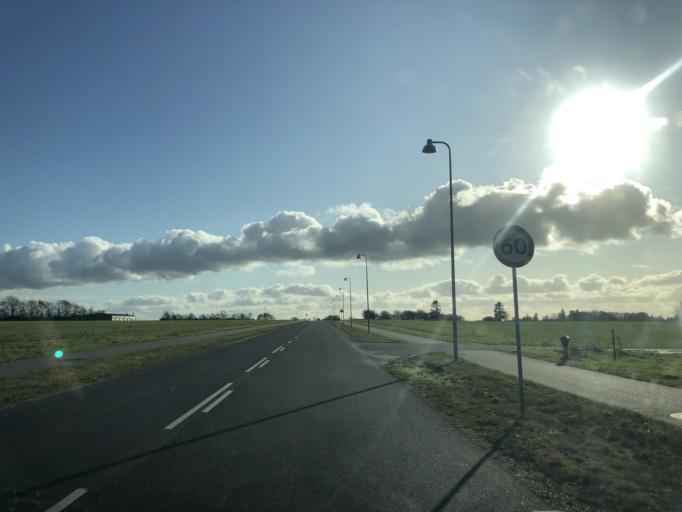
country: DK
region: Central Jutland
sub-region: Ikast-Brande Kommune
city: Bording Kirkeby
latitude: 56.1361
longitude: 9.3430
